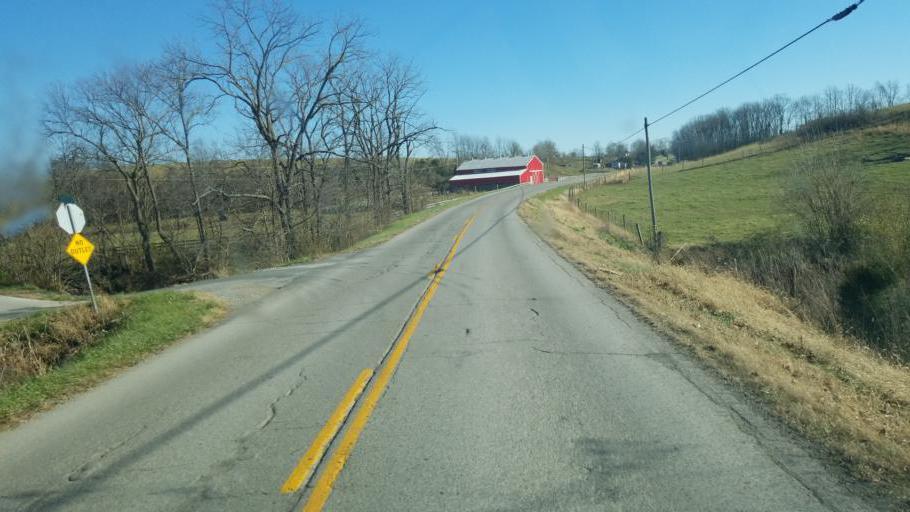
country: US
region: Kentucky
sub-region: Fleming County
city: Flemingsburg
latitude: 38.4898
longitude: -83.6184
